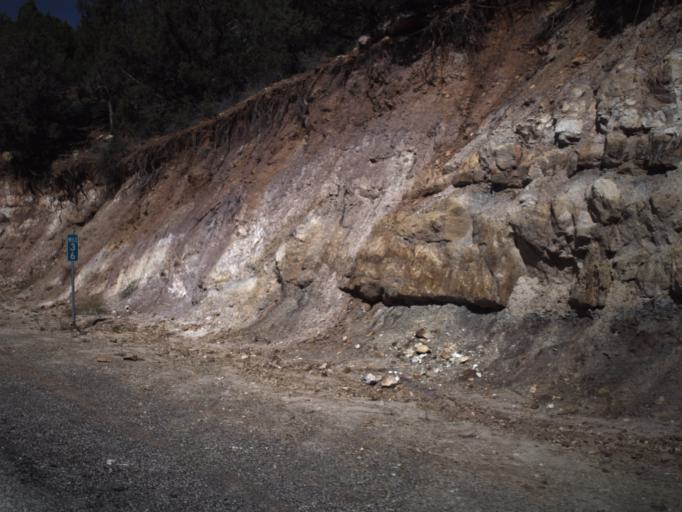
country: US
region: Utah
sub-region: Washington County
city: Enterprise
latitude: 37.5363
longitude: -113.6540
